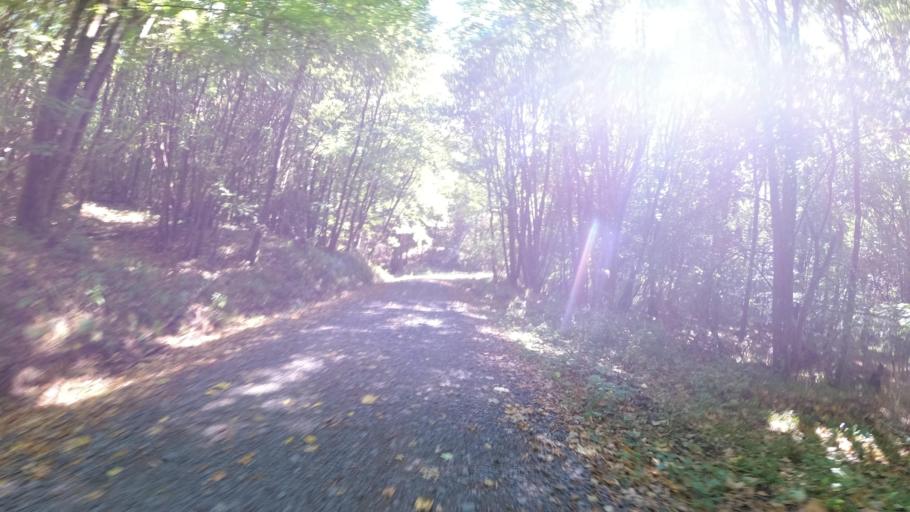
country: DE
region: Saarland
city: Mainzweiler
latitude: 49.4251
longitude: 7.1295
